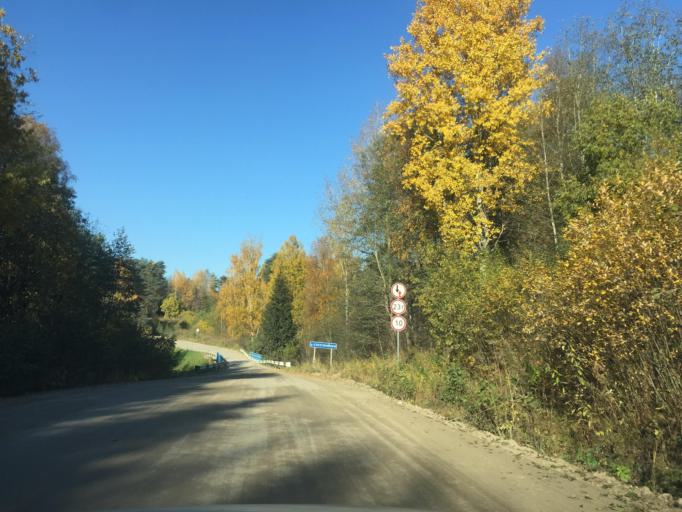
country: RU
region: Leningrad
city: Kuznechnoye
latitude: 61.3231
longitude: 29.9470
